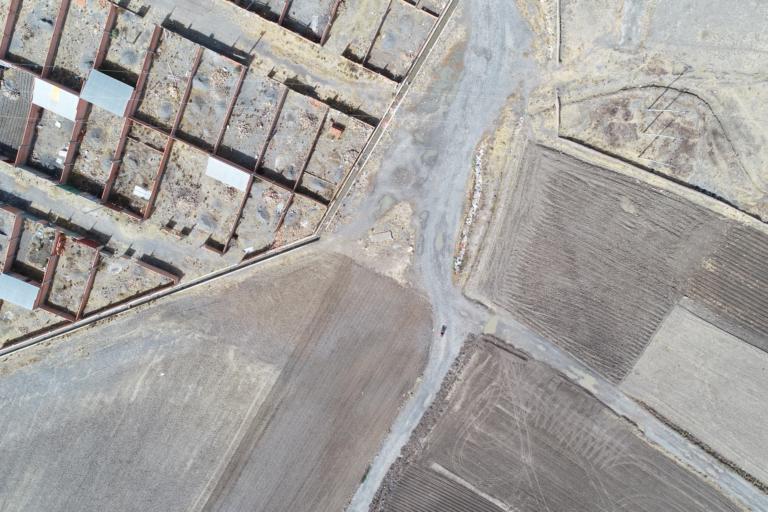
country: BO
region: La Paz
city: Achacachi
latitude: -16.0372
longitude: -68.6843
